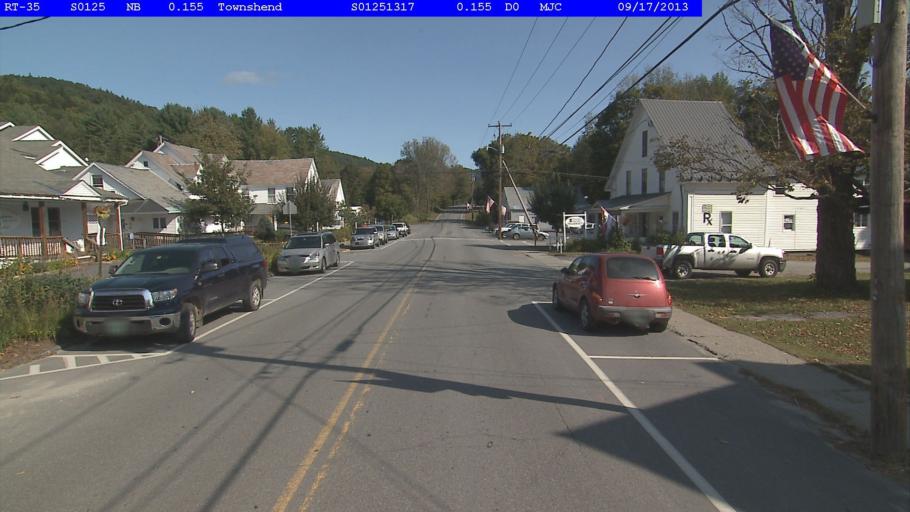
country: US
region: Vermont
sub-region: Windham County
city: Newfane
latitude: 43.0483
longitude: -72.6677
